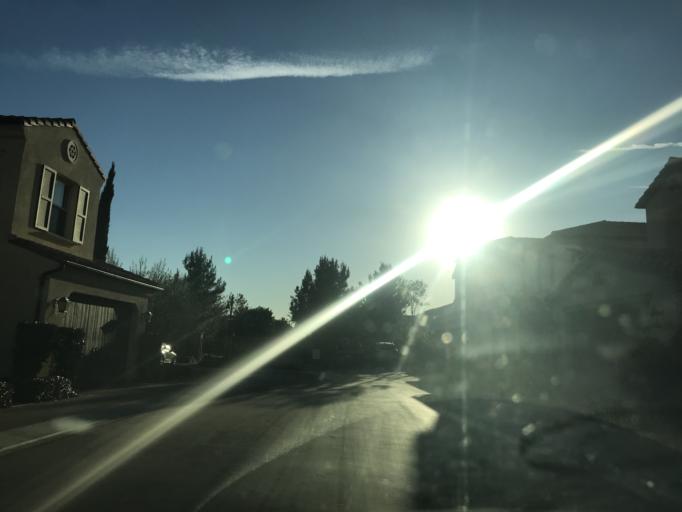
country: US
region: California
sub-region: Orange County
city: North Tustin
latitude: 33.7088
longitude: -117.7453
